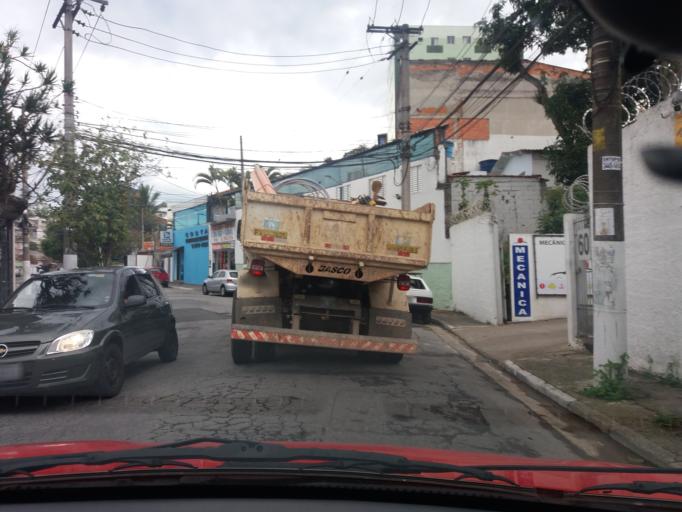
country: BR
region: Sao Paulo
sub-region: Taboao Da Serra
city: Taboao da Serra
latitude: -23.5917
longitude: -46.7419
